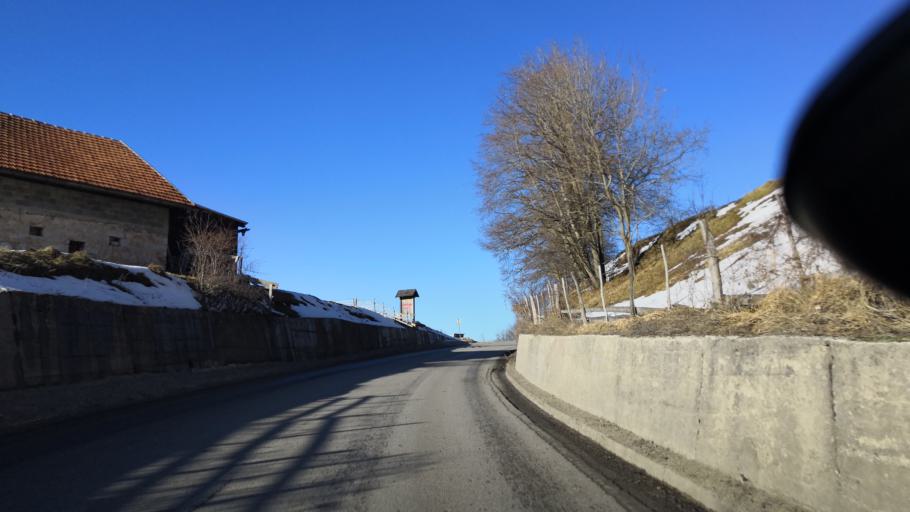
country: BA
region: Republika Srpska
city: Pale
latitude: 43.9043
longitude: 18.6366
